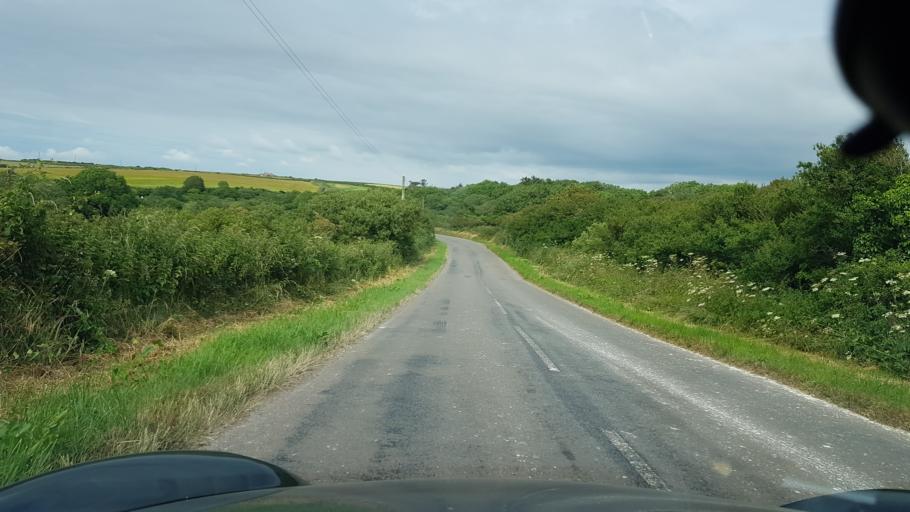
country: GB
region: Wales
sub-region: Pembrokeshire
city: Dale
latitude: 51.7354
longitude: -5.1597
